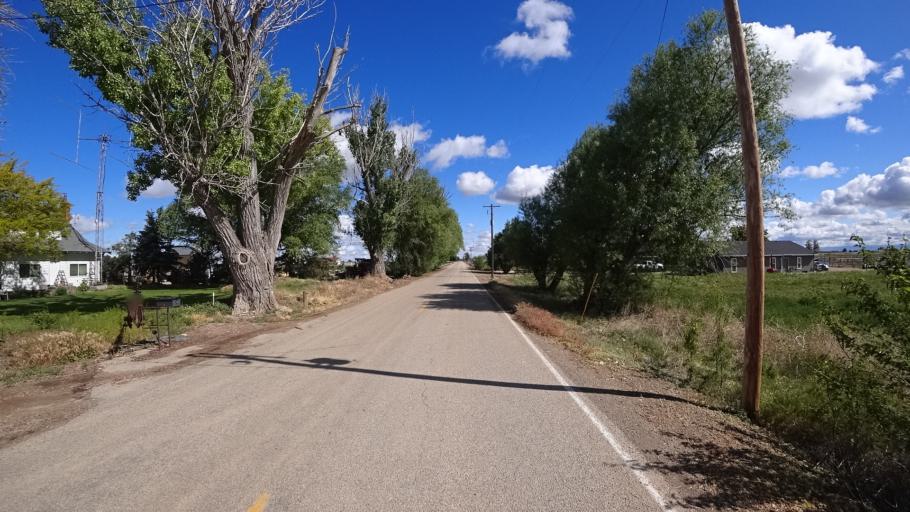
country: US
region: Idaho
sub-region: Ada County
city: Kuna
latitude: 43.4653
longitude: -116.4738
